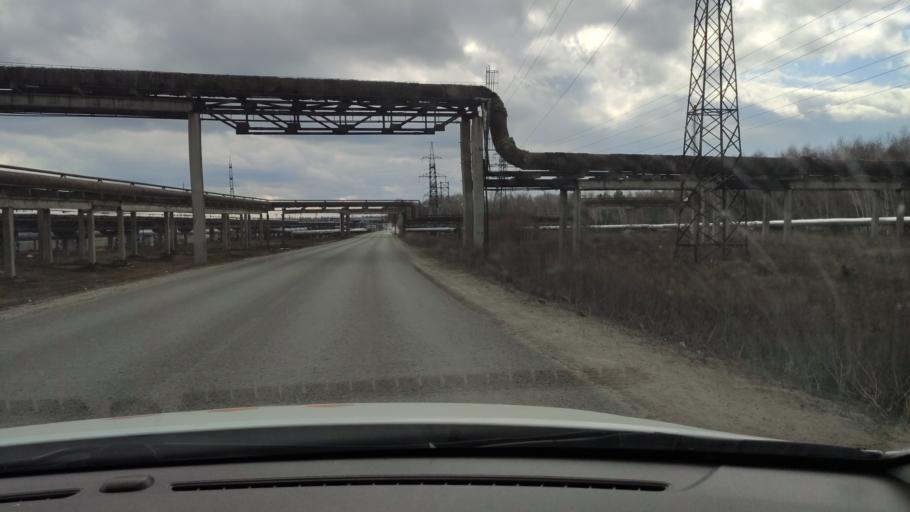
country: RU
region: Tatarstan
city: Staroye Arakchino
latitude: 55.8693
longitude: 48.9735
